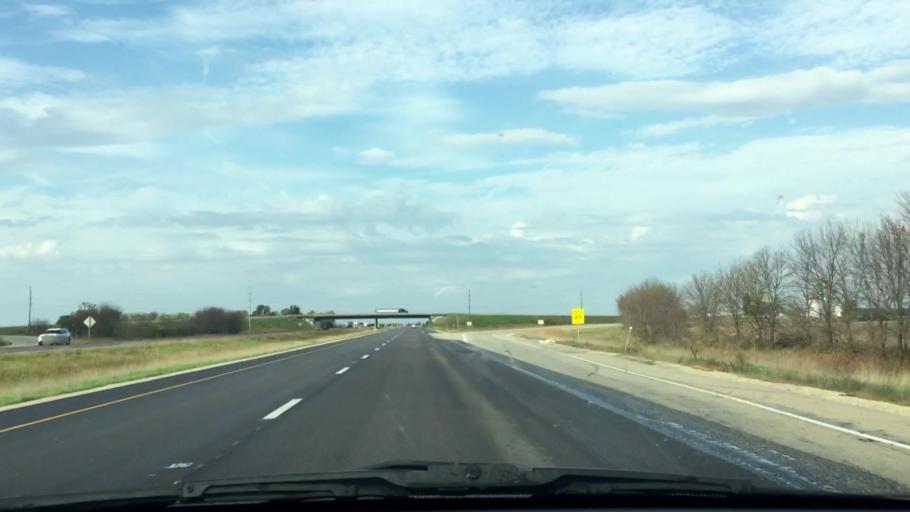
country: US
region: Illinois
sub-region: Whiteside County
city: Erie
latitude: 41.6890
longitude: -90.0919
